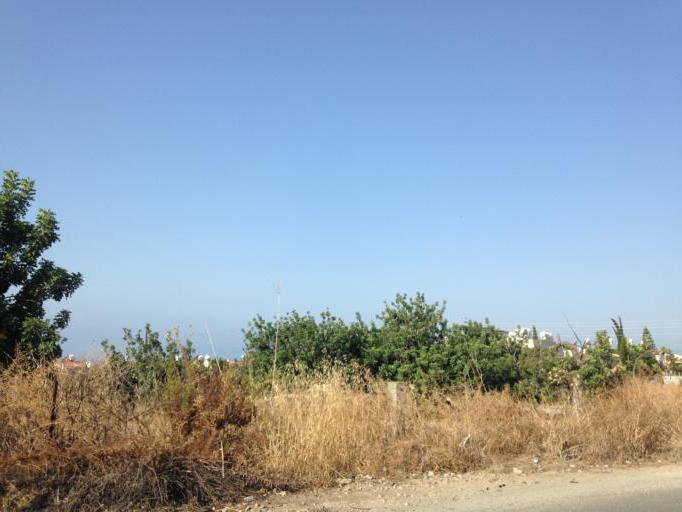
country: CY
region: Pafos
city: Pegeia
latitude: 34.8781
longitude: 32.3855
